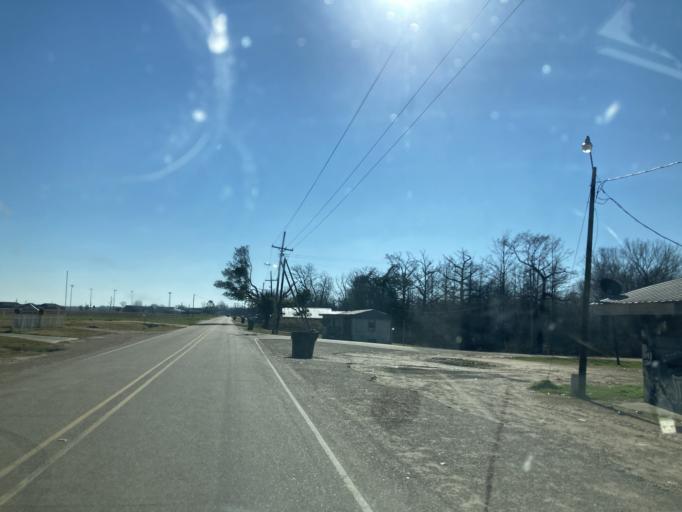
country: US
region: Mississippi
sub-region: Yazoo County
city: Yazoo City
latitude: 32.9779
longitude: -90.5911
